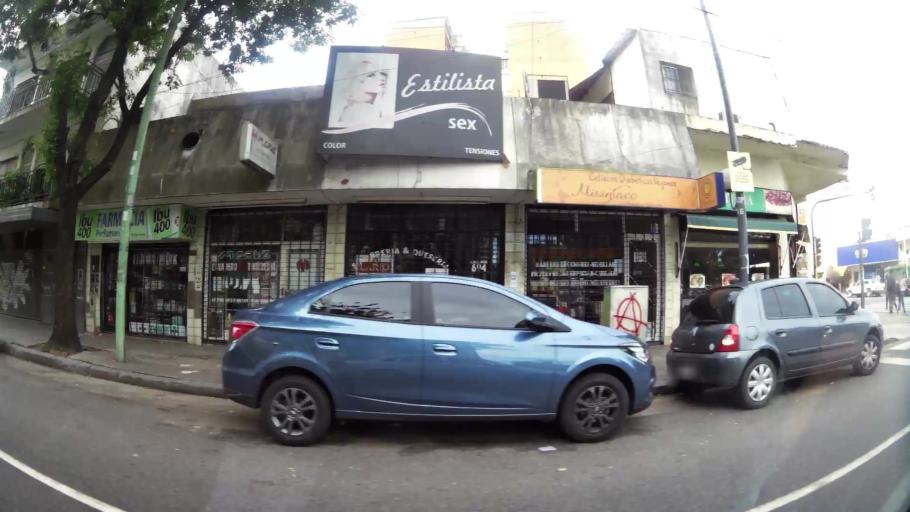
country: AR
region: Buenos Aires F.D.
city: Villa Santa Rita
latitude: -34.6412
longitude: -58.4801
